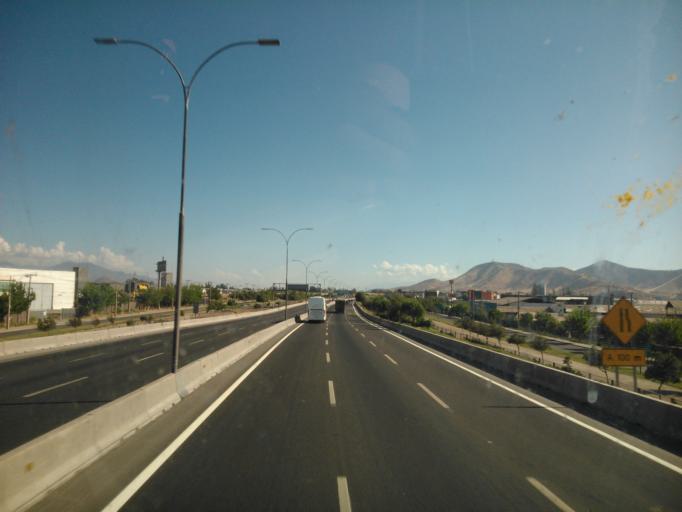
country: CL
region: Santiago Metropolitan
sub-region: Provincia de Maipo
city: San Bernardo
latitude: -33.5455
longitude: -70.7083
